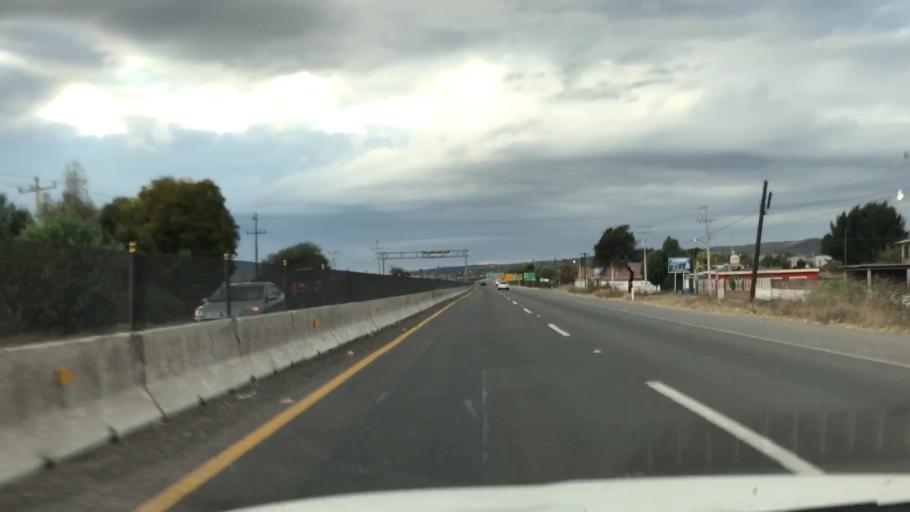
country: MX
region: Guanajuato
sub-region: Penjamo
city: Estacion la Piedad
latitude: 20.3883
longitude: -101.9424
